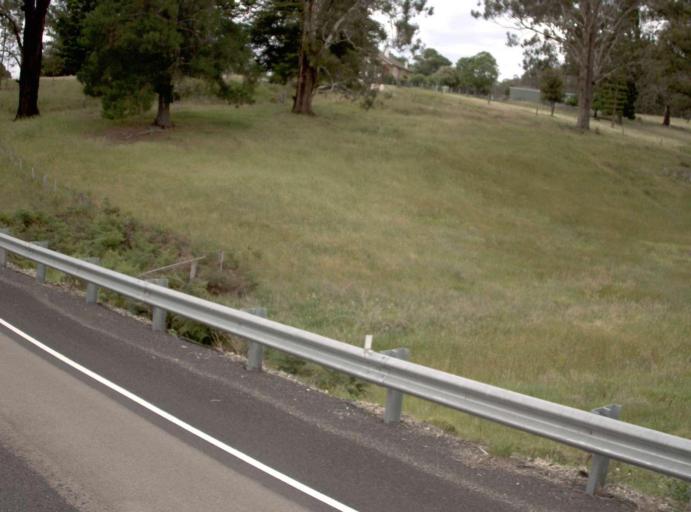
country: AU
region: New South Wales
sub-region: Bombala
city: Bombala
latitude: -37.4844
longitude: 149.1805
